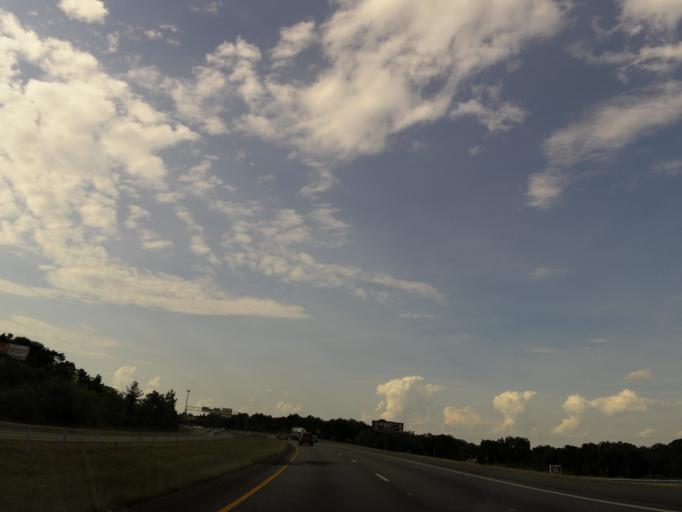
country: US
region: Alabama
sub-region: Jefferson County
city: Brighton
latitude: 33.4273
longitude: -86.9539
